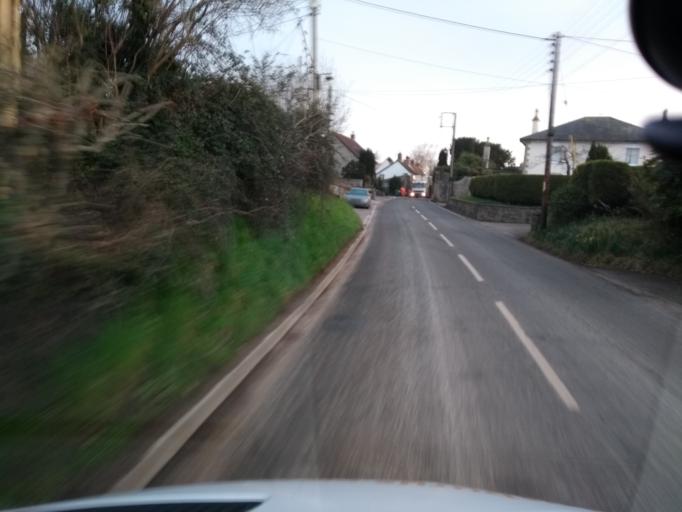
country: GB
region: England
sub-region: Somerset
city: Wedmore
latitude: 51.2254
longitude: -2.8163
